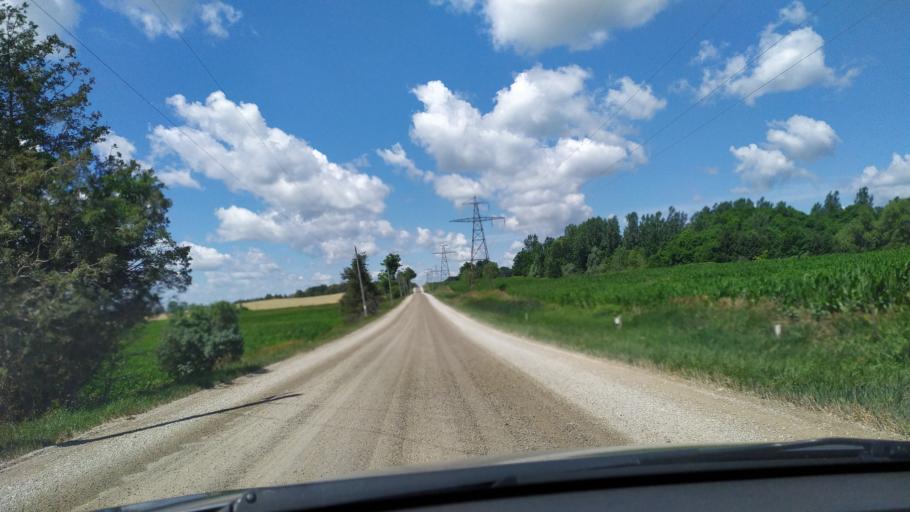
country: CA
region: Ontario
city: Stratford
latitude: 43.3879
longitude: -80.8251
